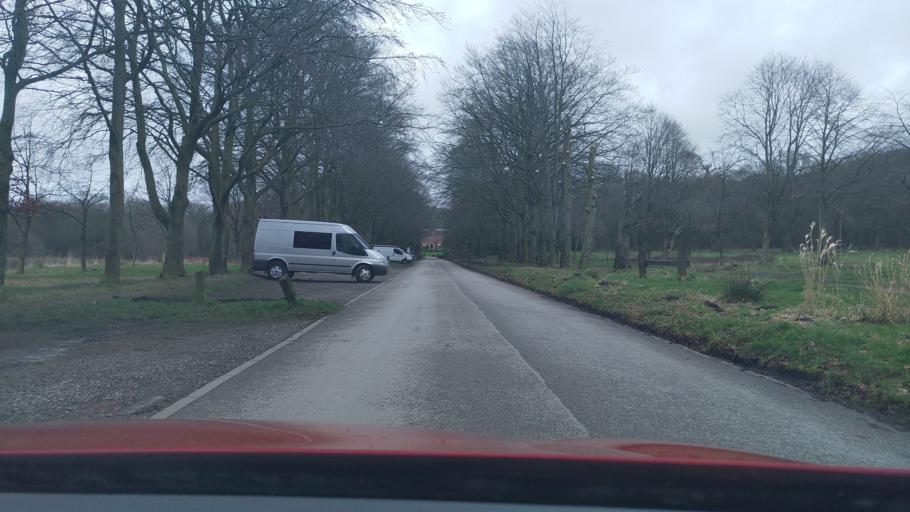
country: GB
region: England
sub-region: Borough of Bolton
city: Horwich
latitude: 53.6232
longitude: -2.5592
